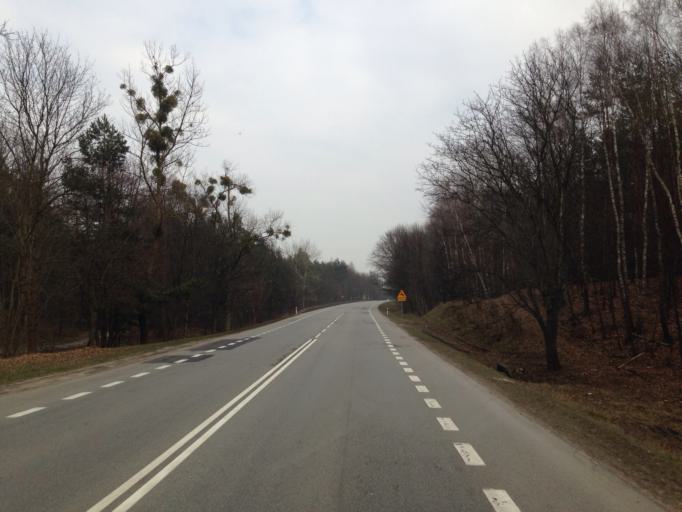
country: PL
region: Pomeranian Voivodeship
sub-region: Powiat tczewski
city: Gniew
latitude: 53.8148
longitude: 18.7964
